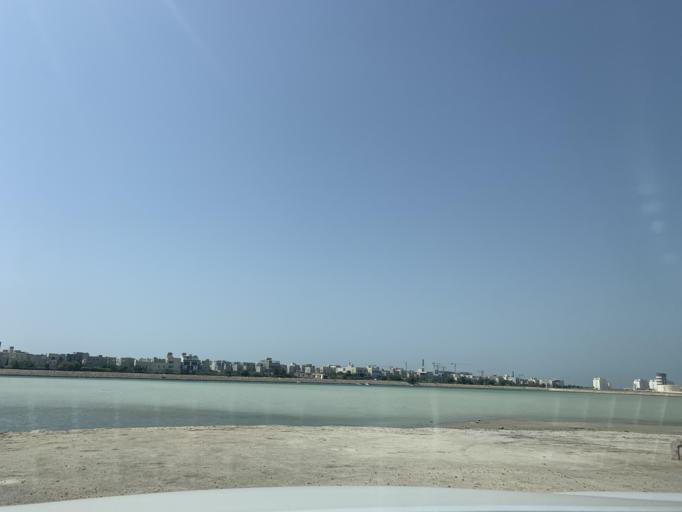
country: BH
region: Manama
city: Jidd Hafs
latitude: 26.2218
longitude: 50.4551
